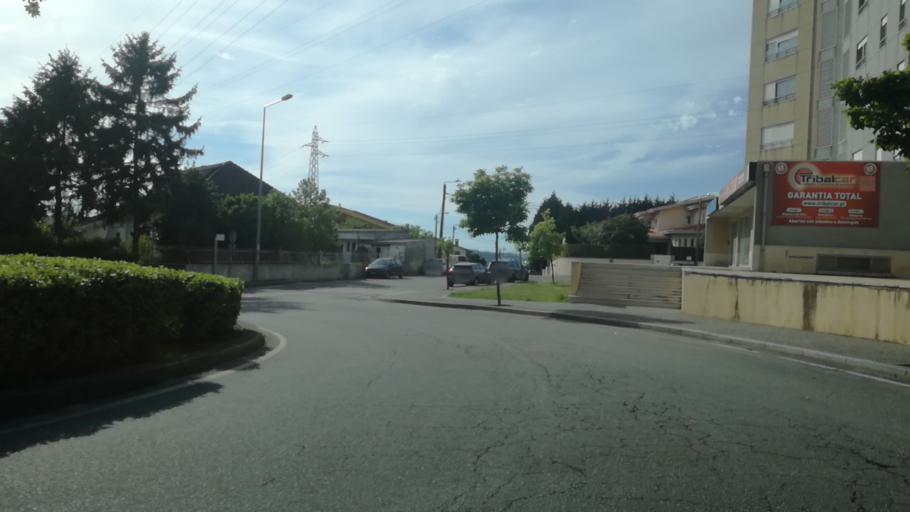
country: PT
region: Porto
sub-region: Maia
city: Nogueira
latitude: 41.2285
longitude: -8.5806
